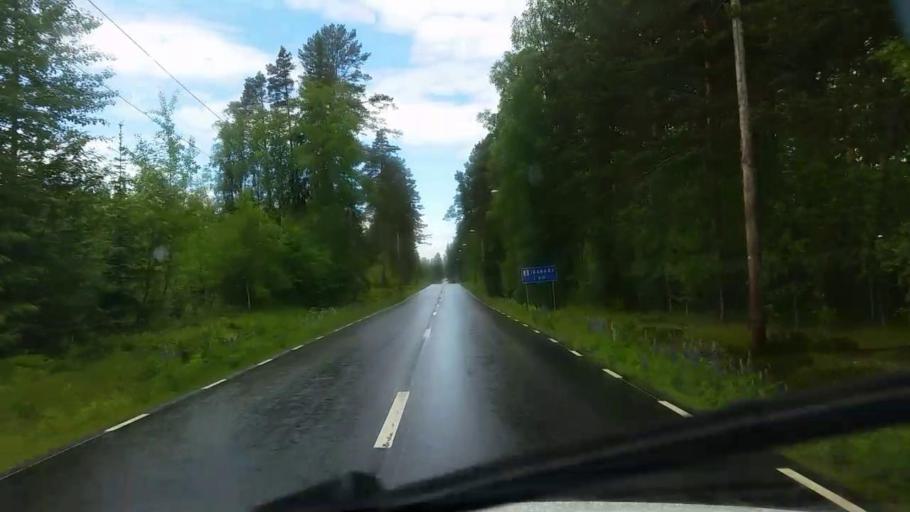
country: SE
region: Gaevleborg
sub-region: Sandvikens Kommun
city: Jarbo
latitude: 60.8380
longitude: 16.4870
